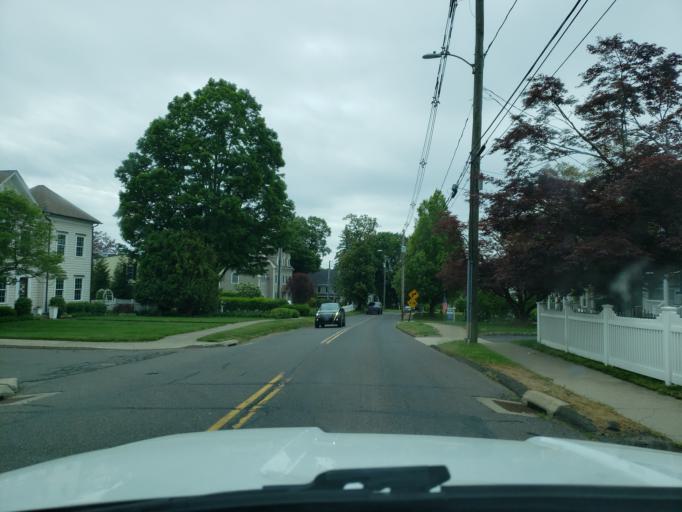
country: US
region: Connecticut
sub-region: Fairfield County
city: Ridgefield
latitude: 41.2834
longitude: -73.5043
